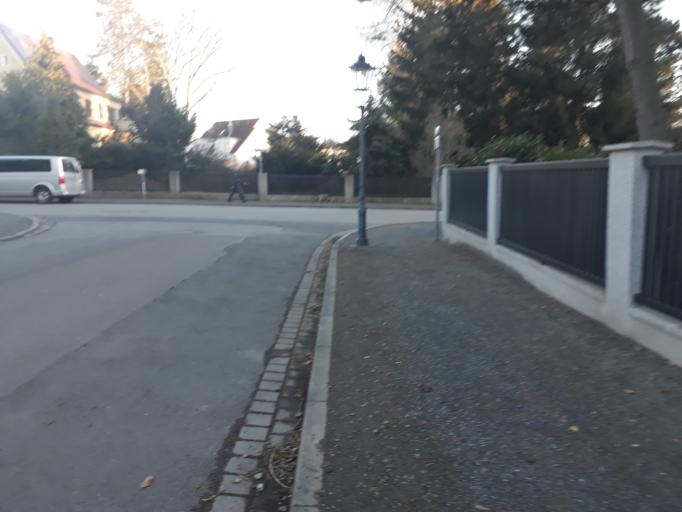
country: DE
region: Saxony
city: Heidenau
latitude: 51.0074
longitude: 13.8561
